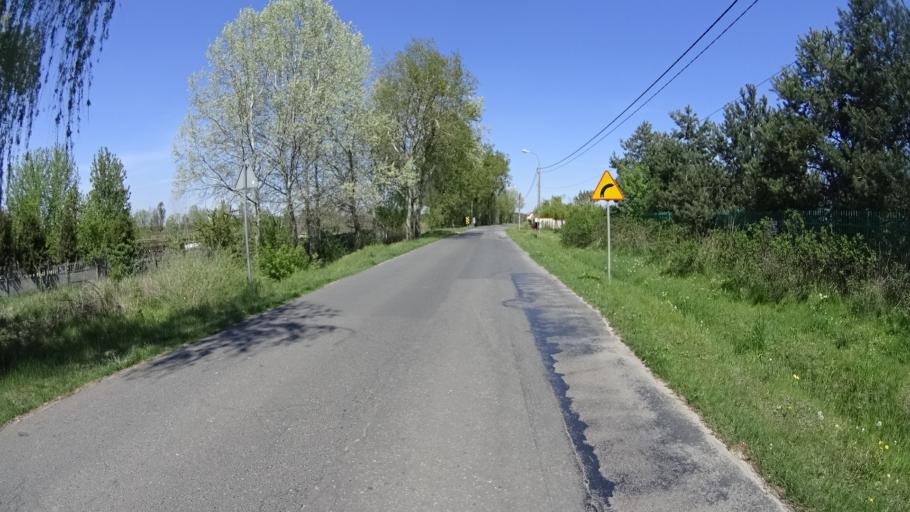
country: PL
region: Masovian Voivodeship
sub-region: Powiat warszawski zachodni
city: Truskaw
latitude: 52.2549
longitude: 20.7346
